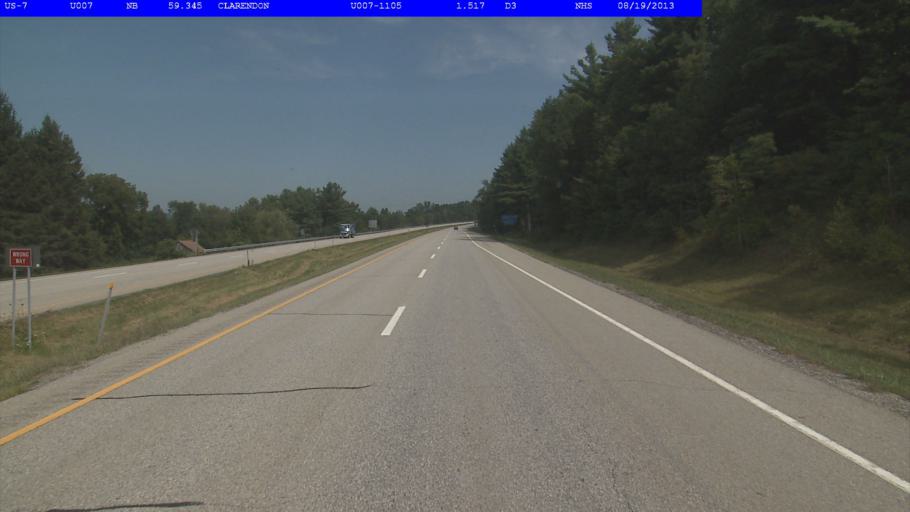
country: US
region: Vermont
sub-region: Rutland County
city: Rutland
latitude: 43.5168
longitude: -72.9675
